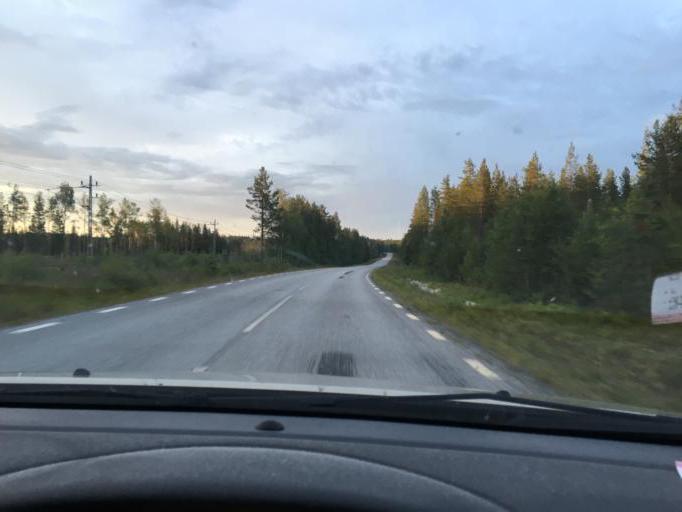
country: SE
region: Norrbotten
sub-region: Lulea Kommun
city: Ranea
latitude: 66.0505
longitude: 22.4092
